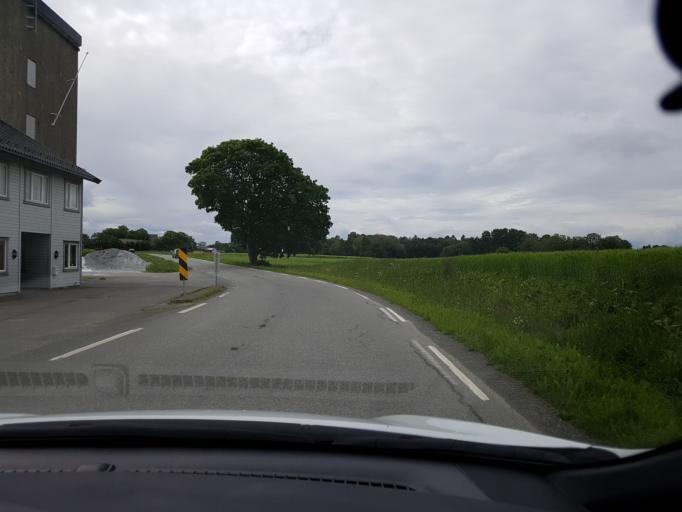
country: NO
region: Nord-Trondelag
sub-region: Frosta
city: Frosta
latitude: 63.5712
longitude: 10.7055
